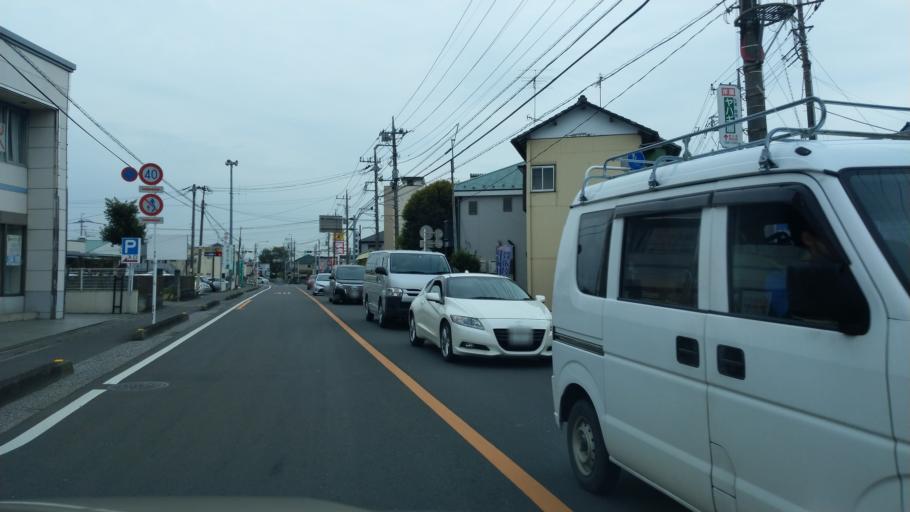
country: JP
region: Saitama
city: Iwatsuki
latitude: 35.9428
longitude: 139.7082
